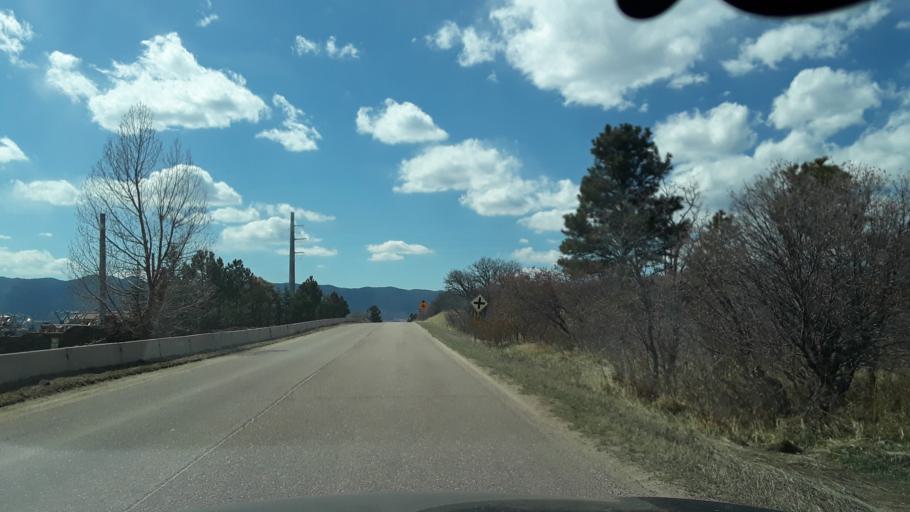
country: US
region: Colorado
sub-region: El Paso County
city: Gleneagle
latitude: 39.0347
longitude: -104.7825
